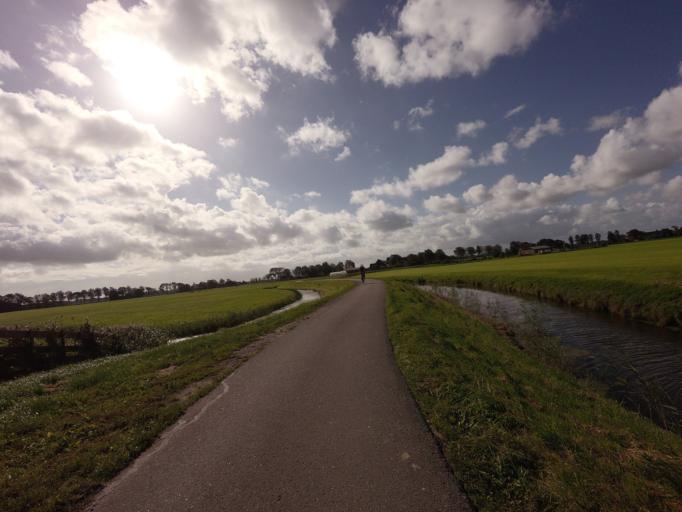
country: NL
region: North Holland
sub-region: Gemeente Hoorn
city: Hoorn
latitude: 52.6734
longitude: 5.0033
